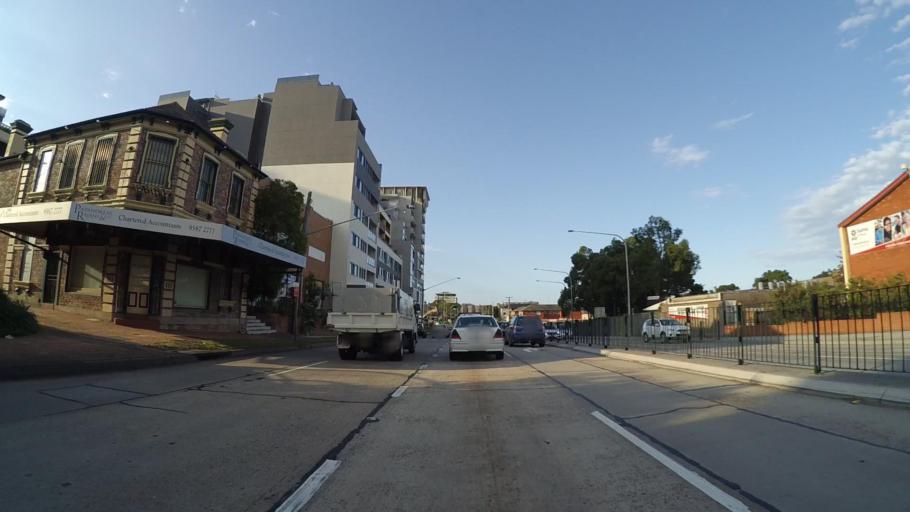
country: AU
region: New South Wales
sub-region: Kogarah
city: Beverly Park
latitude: -33.9654
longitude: 151.1370
